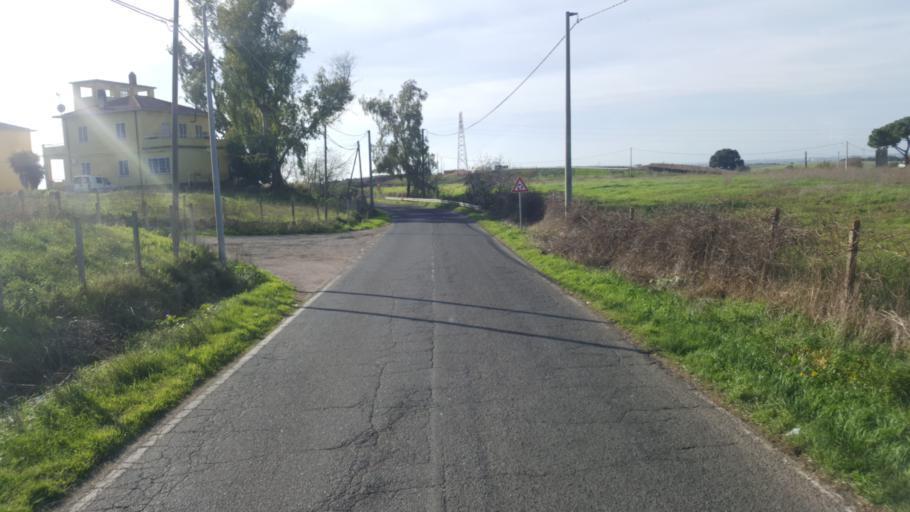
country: IT
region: Latium
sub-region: Citta metropolitana di Roma Capitale
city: Mantiglia di Ardea
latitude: 41.6605
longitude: 12.6300
